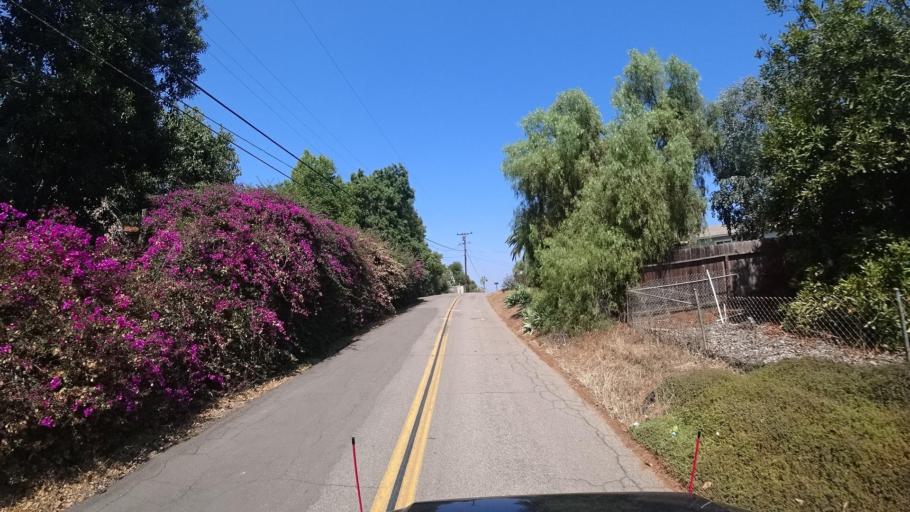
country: US
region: California
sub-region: San Diego County
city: Vista
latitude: 33.2431
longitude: -117.2378
